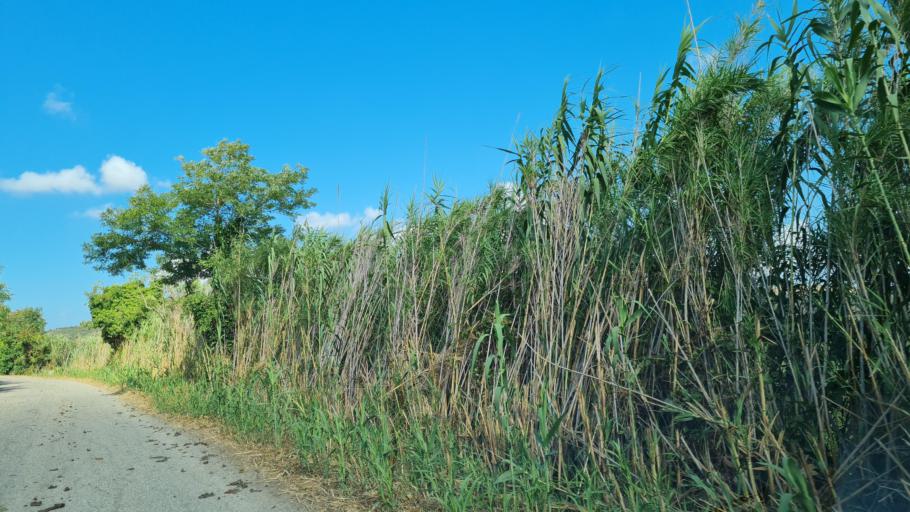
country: IT
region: Latium
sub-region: Provincia di Viterbo
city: Tarquinia
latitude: 42.2608
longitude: 11.7621
